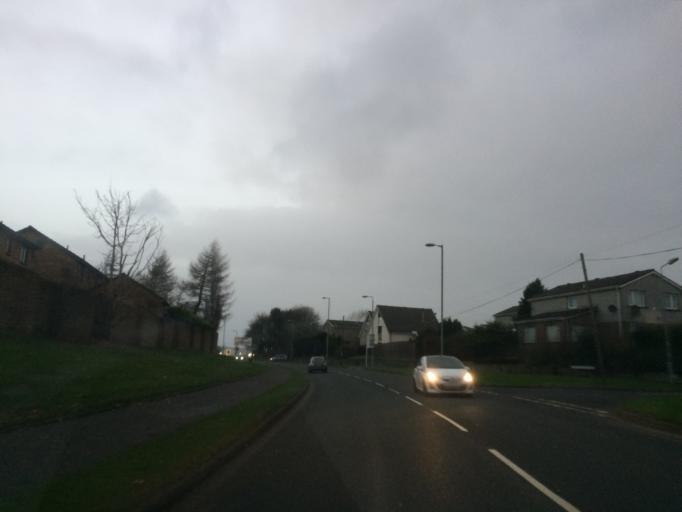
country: GB
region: Scotland
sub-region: East Renfrewshire
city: Newton Mearns
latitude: 55.7818
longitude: -4.3427
